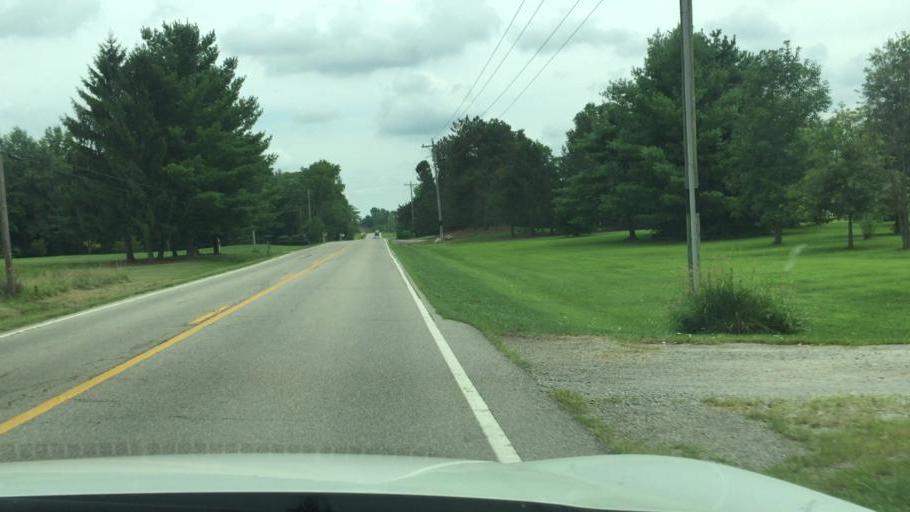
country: US
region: Ohio
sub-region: Union County
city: Marysville
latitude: 40.2293
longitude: -83.4614
